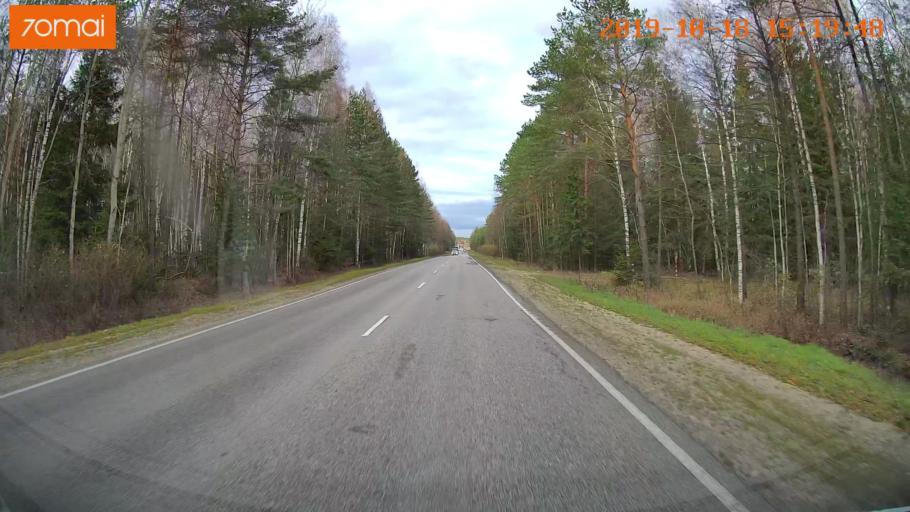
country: RU
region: Vladimir
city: Anopino
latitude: 55.6783
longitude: 40.7403
